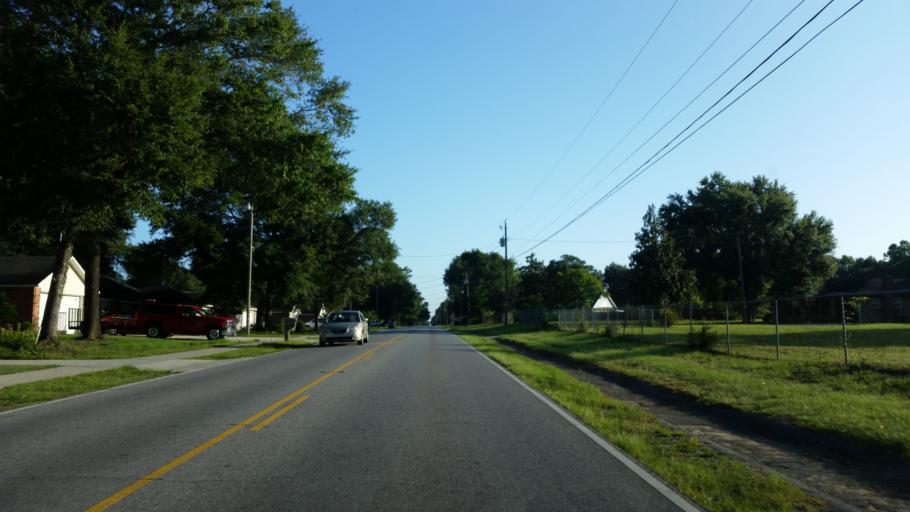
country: US
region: Florida
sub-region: Escambia County
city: Bellview
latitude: 30.4725
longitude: -87.2985
